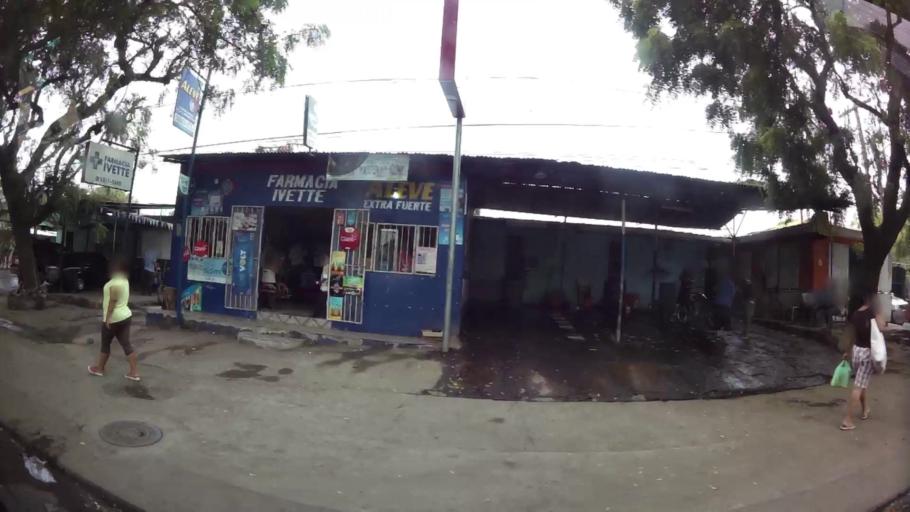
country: NI
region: Leon
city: Leon
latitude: 12.4550
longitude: -86.8694
